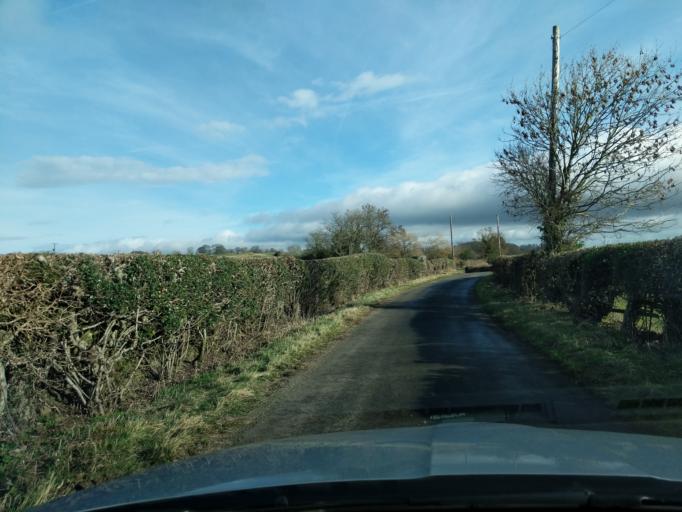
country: GB
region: England
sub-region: North Yorkshire
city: Catterick Garrison
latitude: 54.3340
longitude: -1.7026
